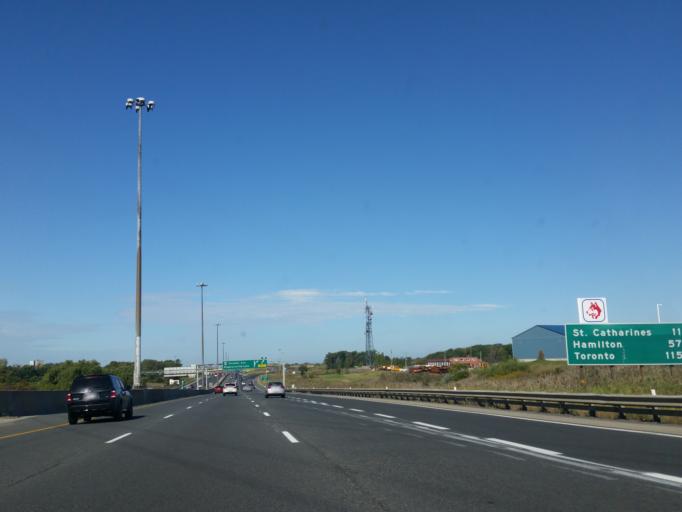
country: CA
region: Ontario
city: Thorold
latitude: 43.1536
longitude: -79.1542
